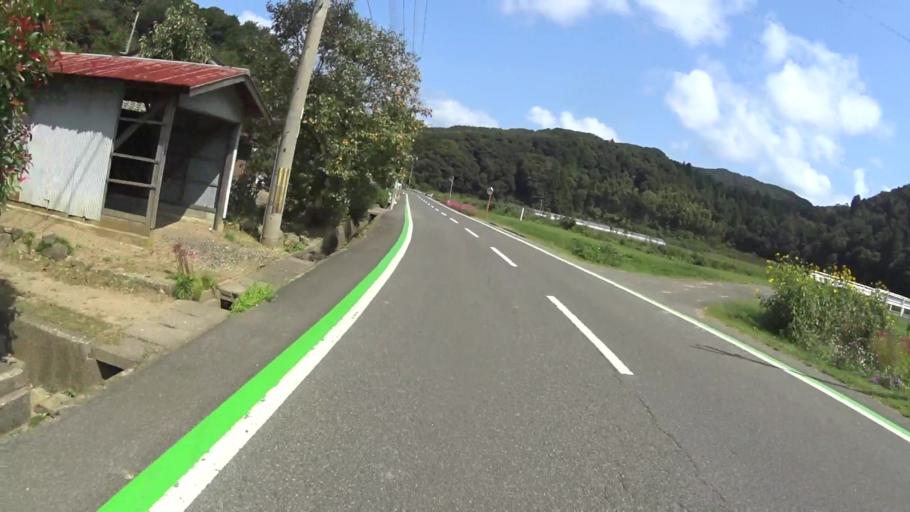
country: JP
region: Kyoto
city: Miyazu
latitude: 35.7138
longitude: 135.2520
